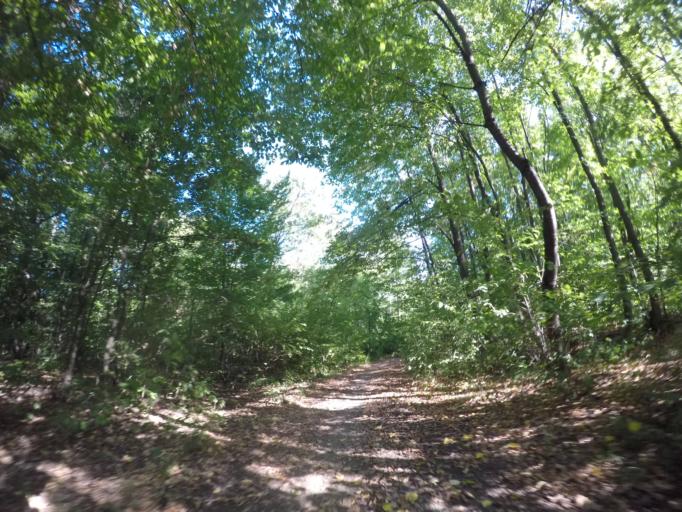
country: SK
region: Kosicky
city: Kosice
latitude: 48.7425
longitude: 21.2088
